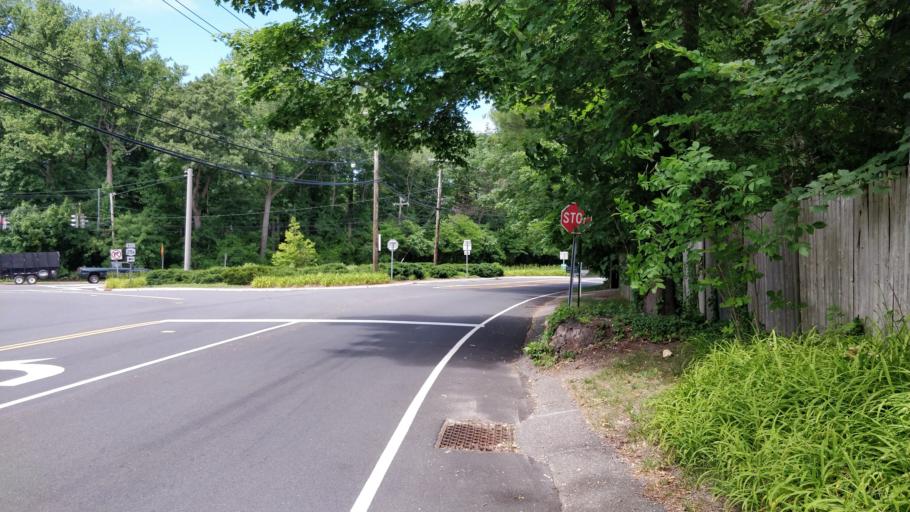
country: US
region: New York
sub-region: Nassau County
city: Laurel Hollow
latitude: 40.8505
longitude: -73.4745
